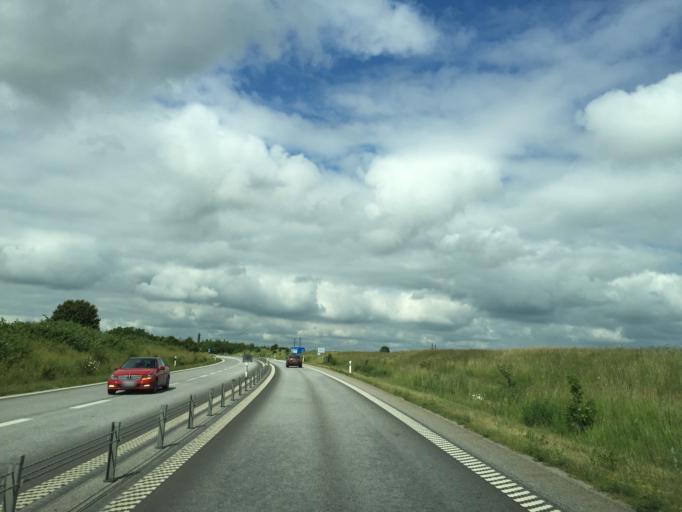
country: SE
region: Skane
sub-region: Staffanstorps Kommun
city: Hjaerup
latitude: 55.7082
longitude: 13.1469
